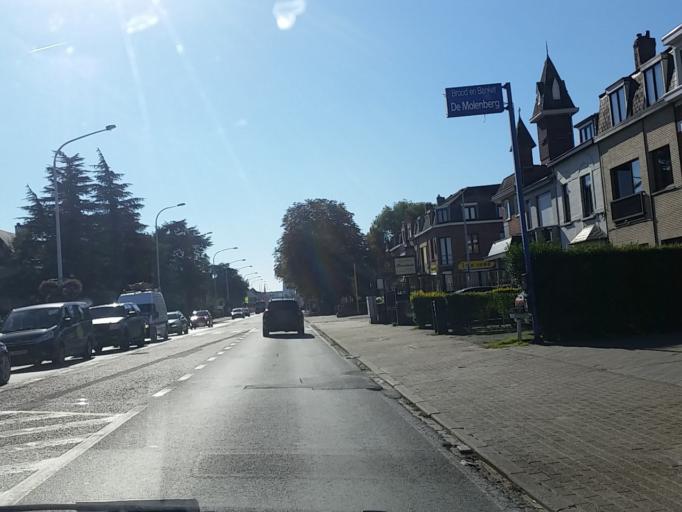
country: BE
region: Flanders
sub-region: Provincie Antwerpen
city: Mechelen
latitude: 51.0427
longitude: 4.4704
